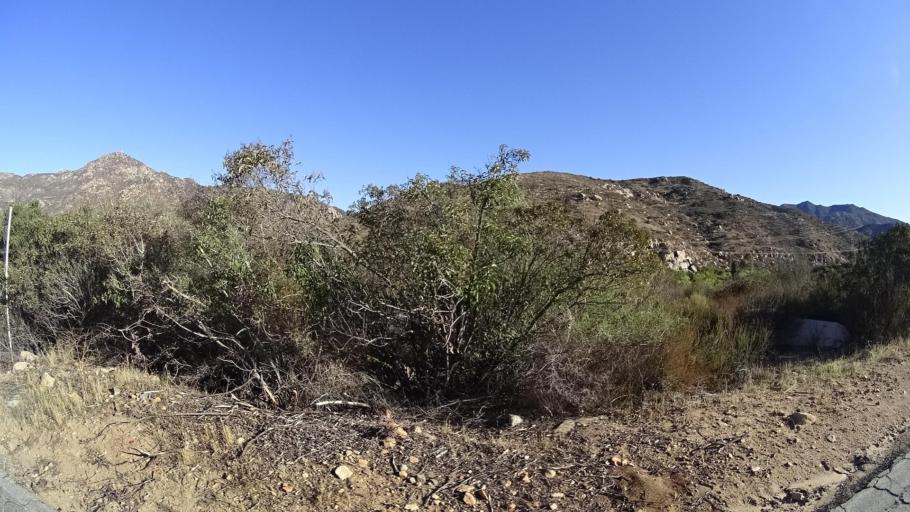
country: MX
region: Baja California
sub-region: Tecate
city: Lomas de Santa Anita
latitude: 32.6040
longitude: -116.6907
